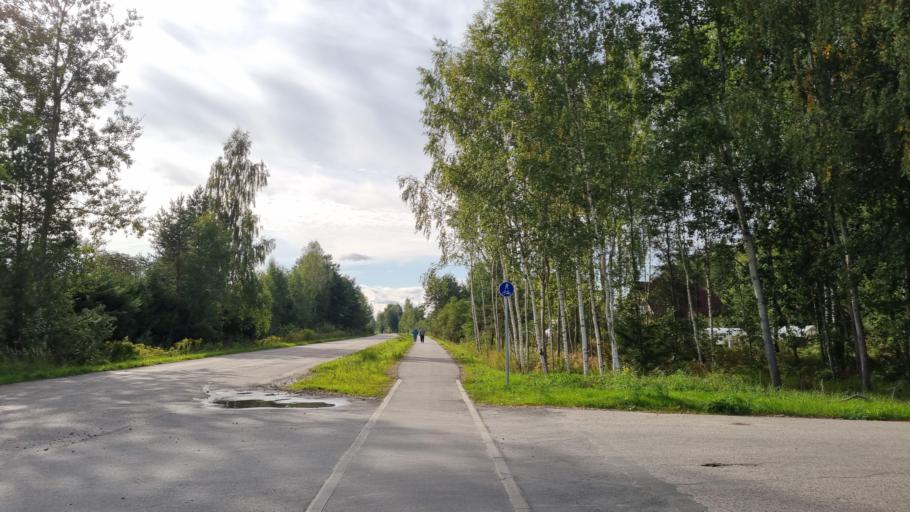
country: LV
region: Olaine
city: Olaine
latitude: 56.6994
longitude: 24.0671
